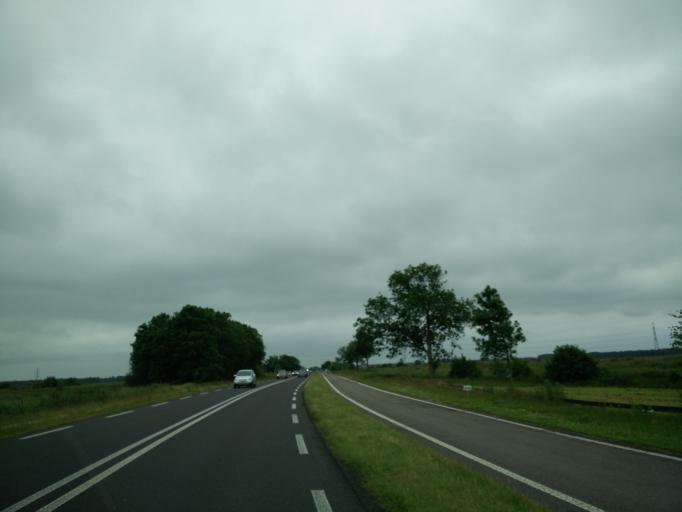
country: NL
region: Groningen
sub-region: Gemeente Groningen
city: Groningen
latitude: 53.1830
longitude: 6.5088
